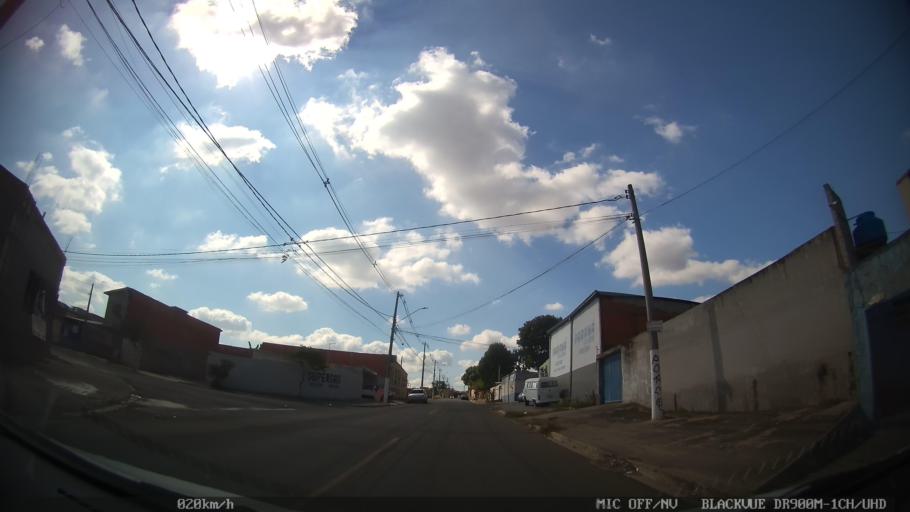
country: BR
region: Sao Paulo
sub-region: Hortolandia
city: Hortolandia
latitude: -22.8815
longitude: -47.2081
